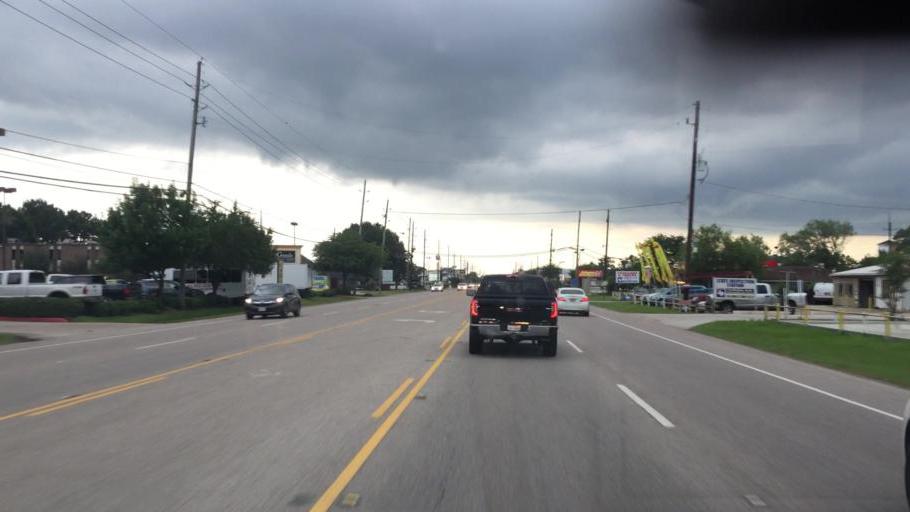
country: US
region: Texas
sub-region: Harris County
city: Spring
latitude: 30.0372
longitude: -95.4944
